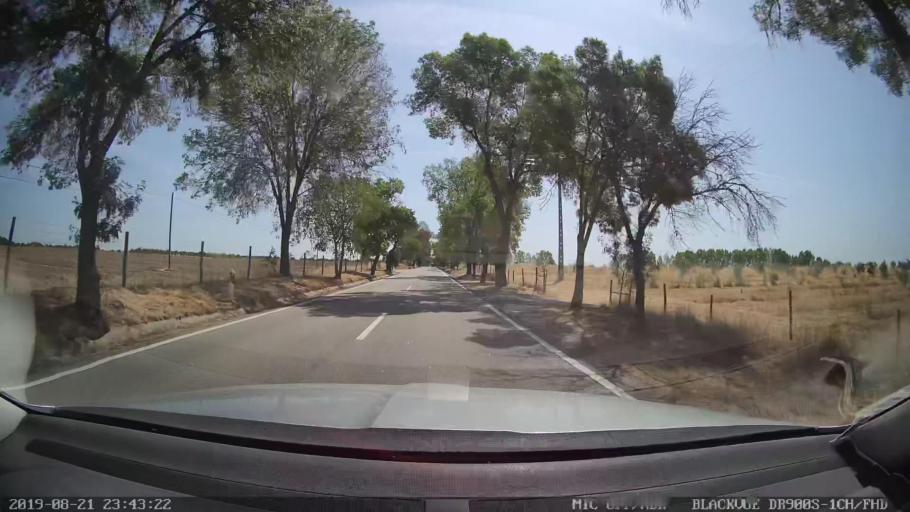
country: PT
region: Castelo Branco
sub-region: Idanha-A-Nova
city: Idanha-a-Nova
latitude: 39.8502
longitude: -7.2958
